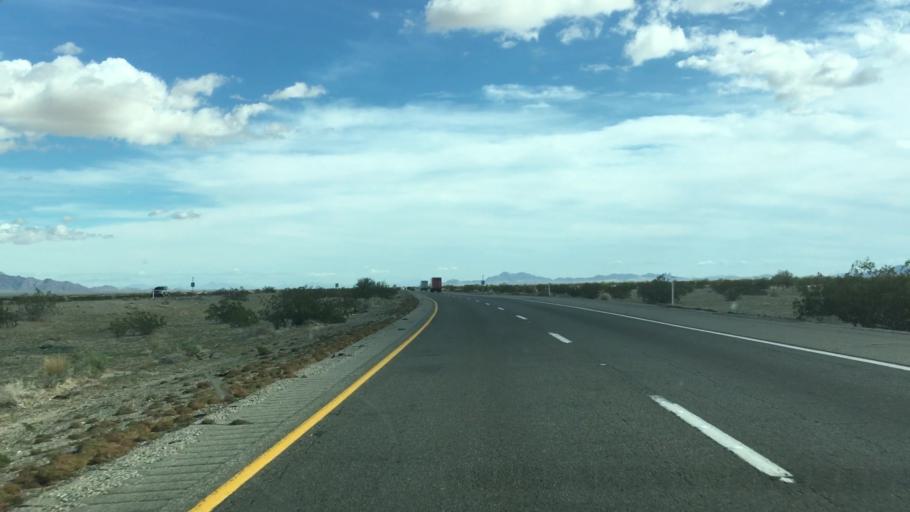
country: US
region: California
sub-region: Riverside County
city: Mesa Verde
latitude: 33.6303
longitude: -115.0731
